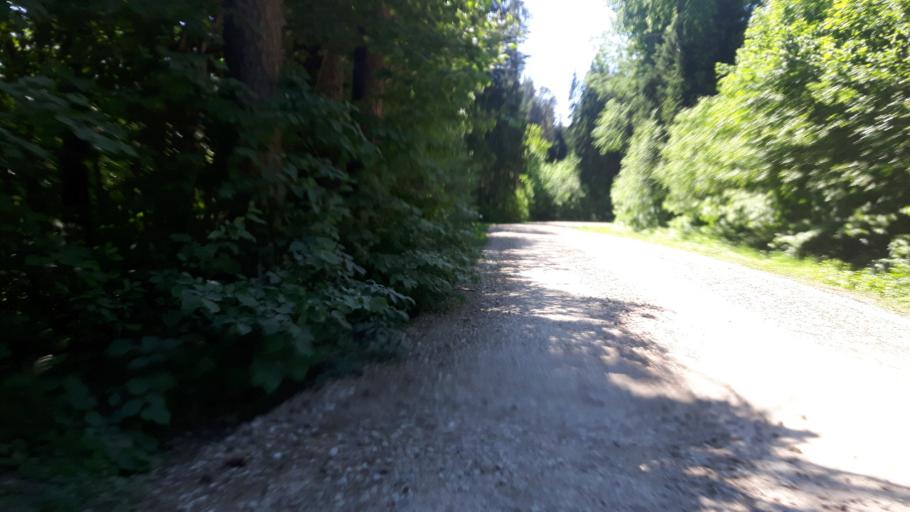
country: EE
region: Paernumaa
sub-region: Tootsi vald
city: Tootsi
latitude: 58.5077
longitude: 24.9079
